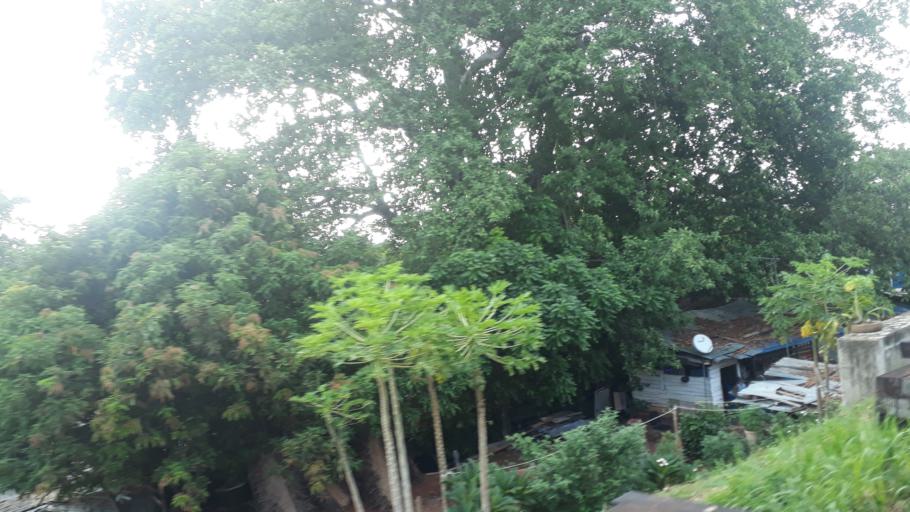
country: LK
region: Western
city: Peliyagoda
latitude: 6.9532
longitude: 79.8897
